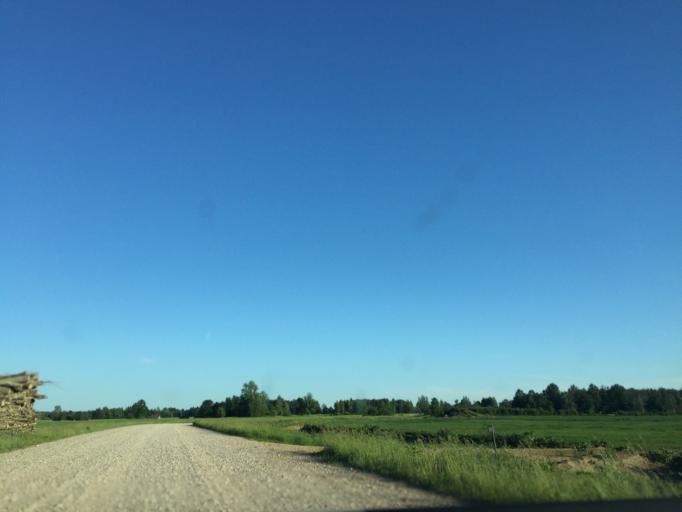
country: LV
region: Broceni
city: Broceni
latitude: 56.8452
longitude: 22.5659
